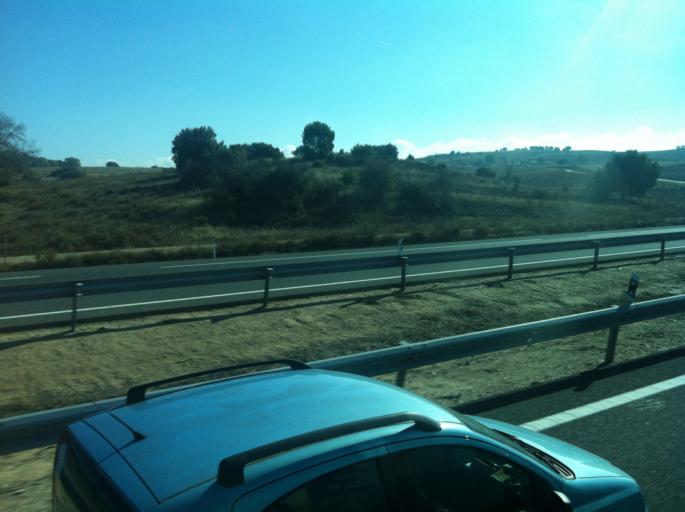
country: ES
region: Castille and Leon
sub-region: Provincia de Burgos
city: Aranda de Duero
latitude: 41.7017
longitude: -3.7027
